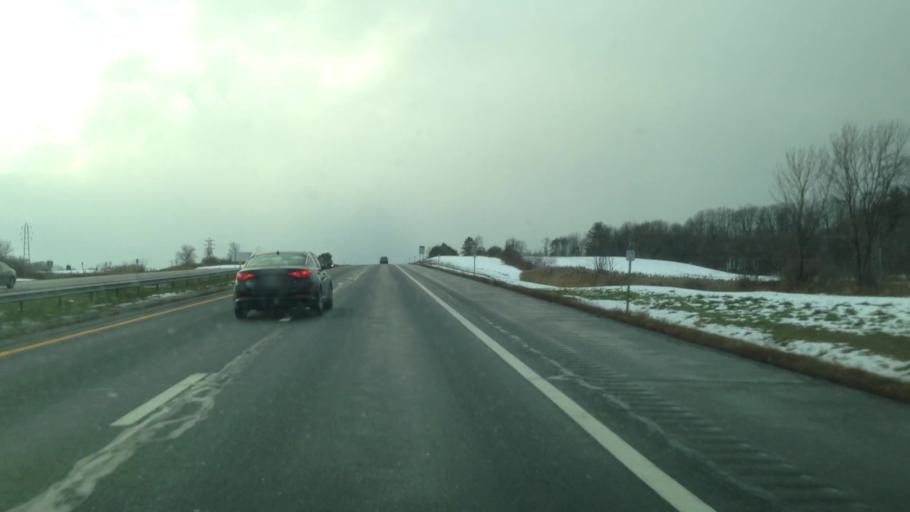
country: US
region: New York
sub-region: Montgomery County
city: Amsterdam
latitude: 42.9300
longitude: -74.2288
